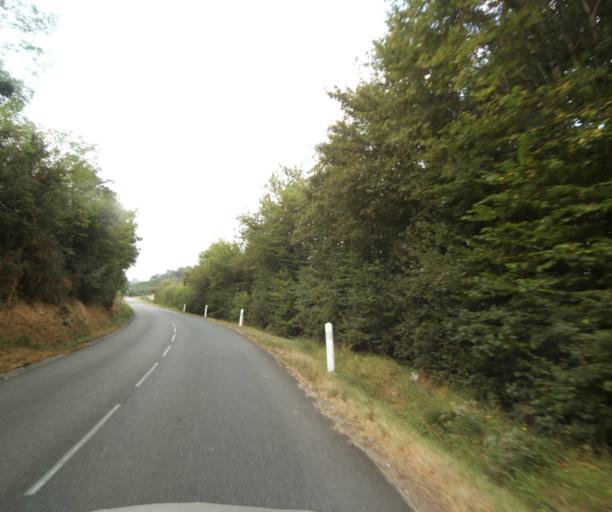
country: FR
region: Aquitaine
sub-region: Departement de la Gironde
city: Creon
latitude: 44.7632
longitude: -0.3622
